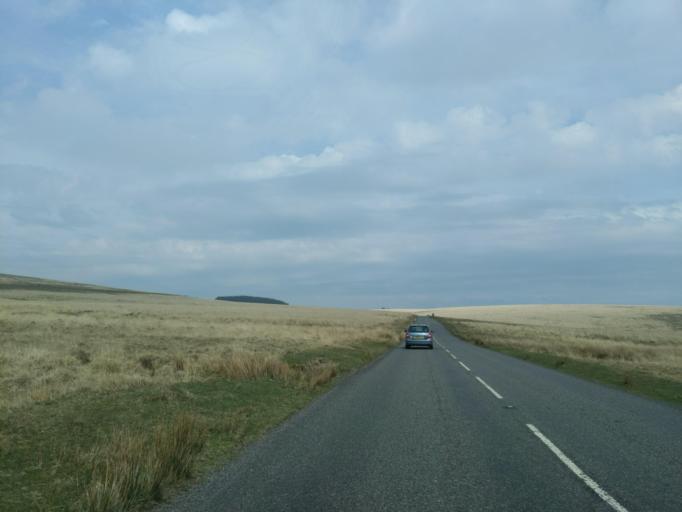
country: GB
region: England
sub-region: Devon
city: Yelverton
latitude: 50.5358
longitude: -4.0108
